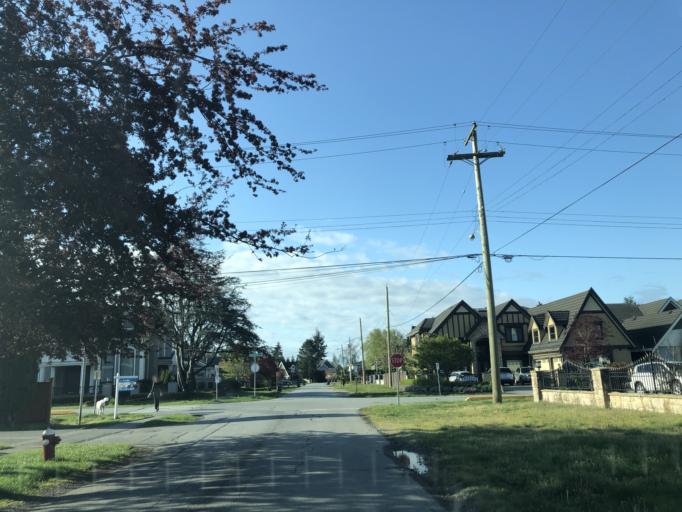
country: CA
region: British Columbia
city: Richmond
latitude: 49.1435
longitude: -123.1156
